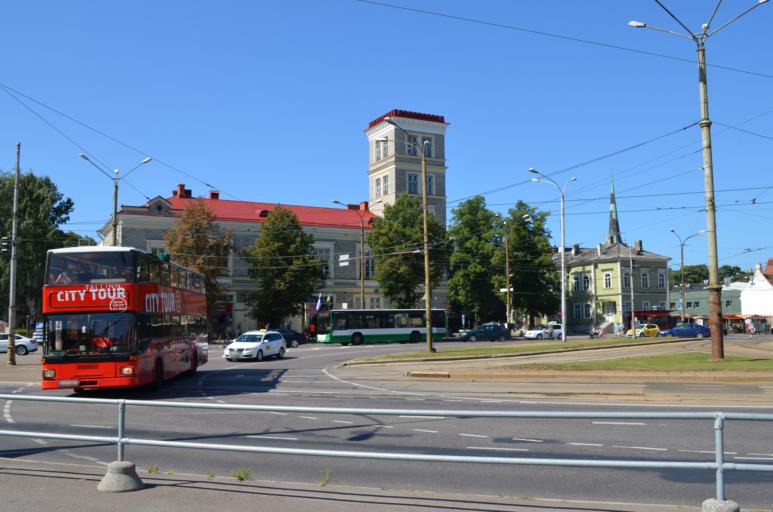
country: EE
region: Harju
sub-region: Tallinna linn
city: Tallinn
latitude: 59.4368
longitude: 24.7535
